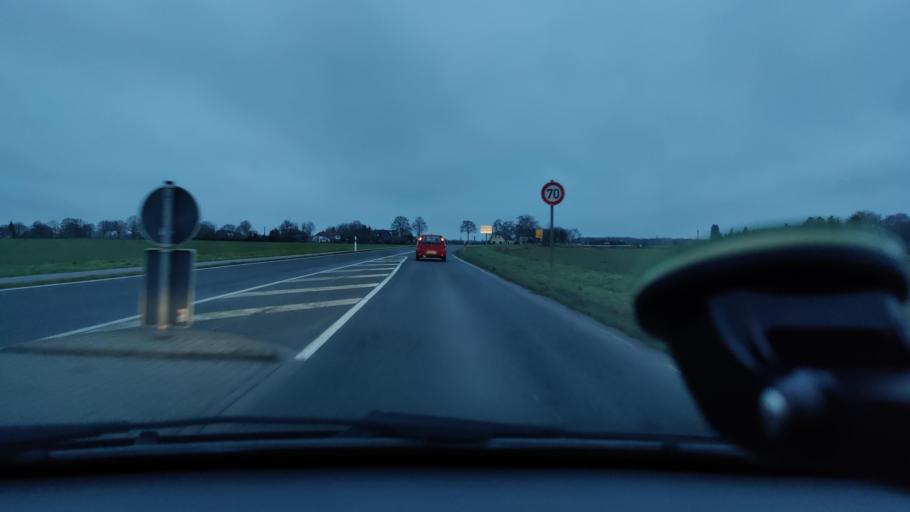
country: DE
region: North Rhine-Westphalia
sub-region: Regierungsbezirk Dusseldorf
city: Xanten
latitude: 51.6680
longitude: 6.4336
